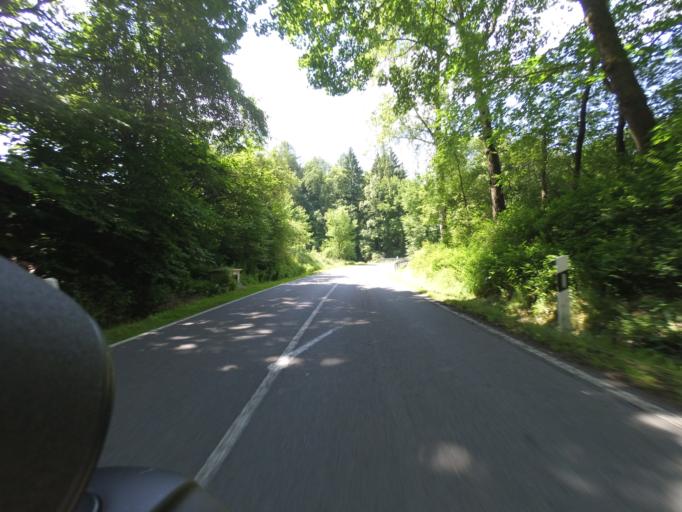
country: DE
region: Saxony
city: Hohnstein
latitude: 50.9822
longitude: 14.1063
